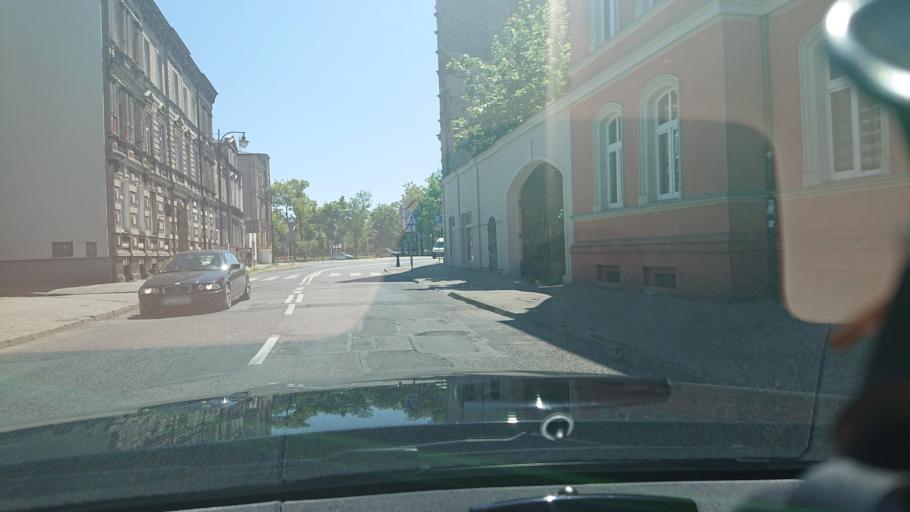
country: PL
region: Greater Poland Voivodeship
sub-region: Powiat gnieznienski
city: Gniezno
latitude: 52.5315
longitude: 17.5984
